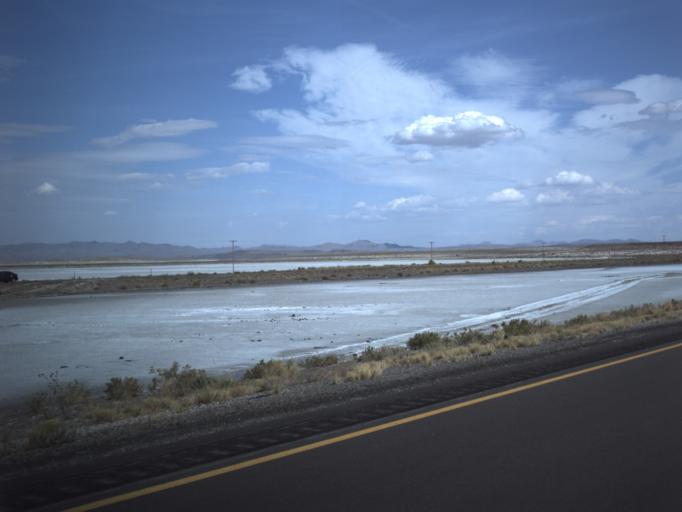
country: US
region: Utah
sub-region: Tooele County
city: Wendover
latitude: 40.7266
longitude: -113.2686
